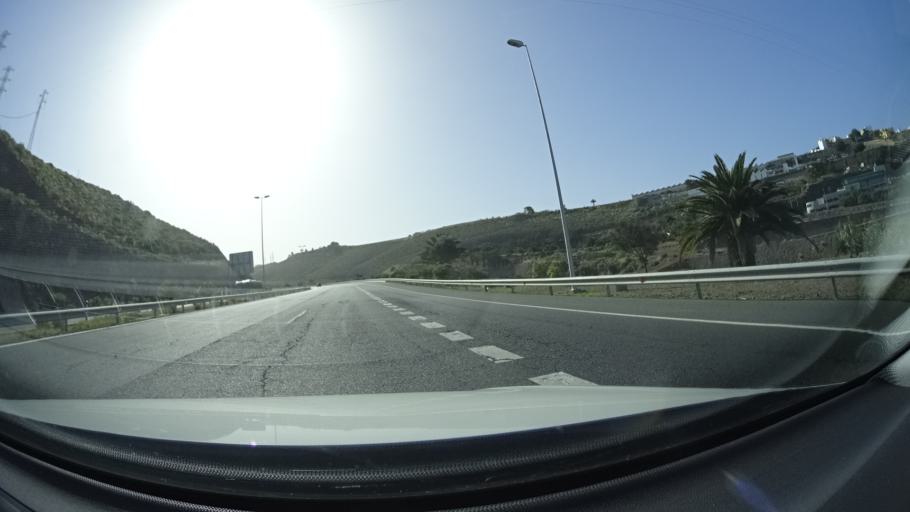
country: ES
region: Canary Islands
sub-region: Provincia de Las Palmas
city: Las Palmas de Gran Canaria
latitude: 28.0839
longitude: -15.4321
